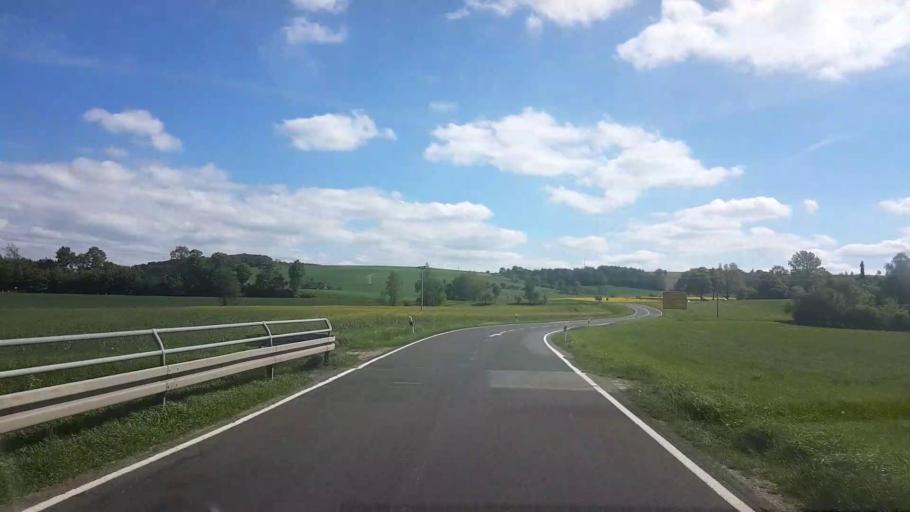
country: DE
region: Bavaria
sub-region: Regierungsbezirk Unterfranken
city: Untermerzbach
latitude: 50.1291
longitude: 10.8844
